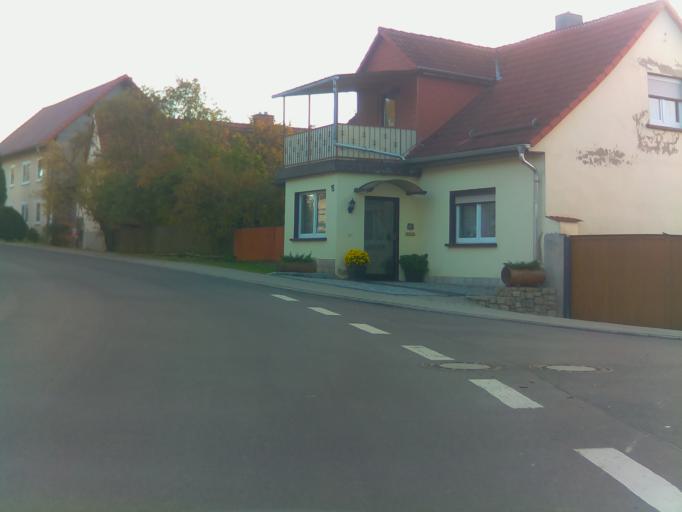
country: DE
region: Thuringia
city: Elleben
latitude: 50.8787
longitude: 11.1179
